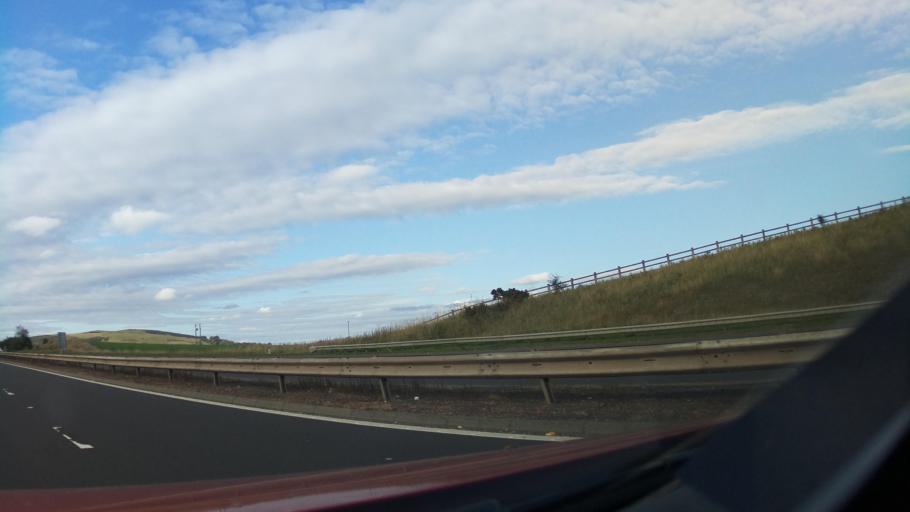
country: GB
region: Scotland
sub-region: Fife
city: Crossgates
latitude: 56.0708
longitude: -3.3902
